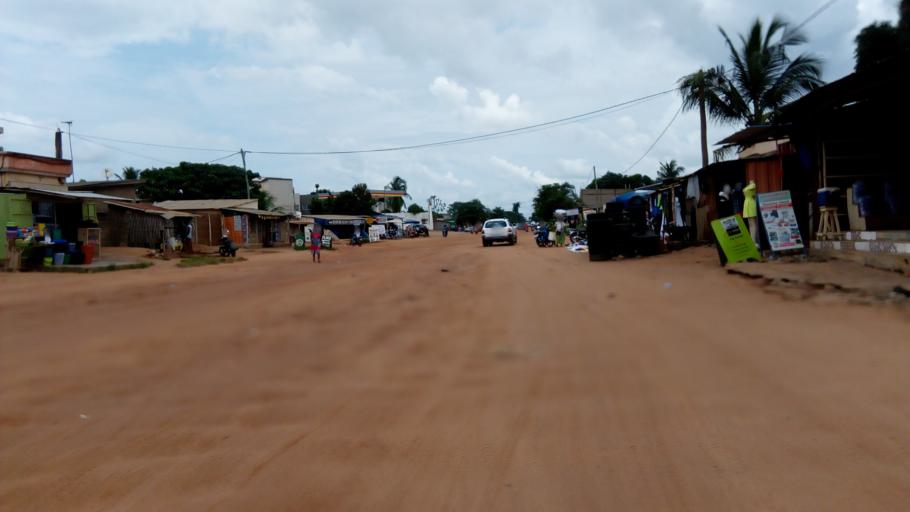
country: TG
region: Maritime
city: Lome
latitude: 6.2200
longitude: 1.1674
